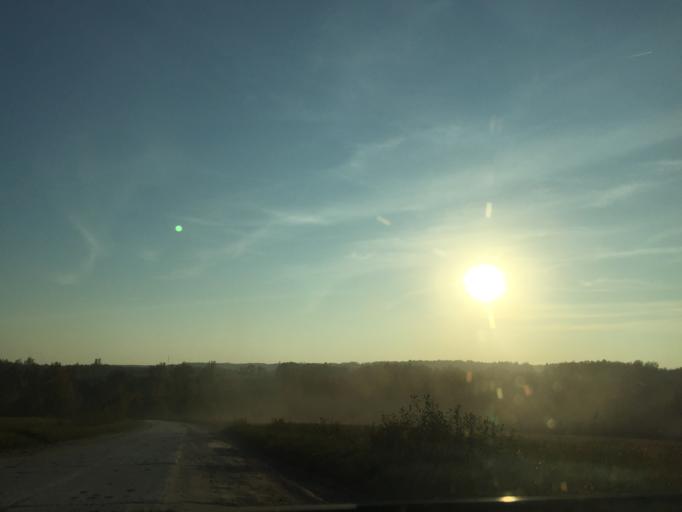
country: LV
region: Vainode
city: Vainode
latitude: 56.5299
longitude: 21.8289
